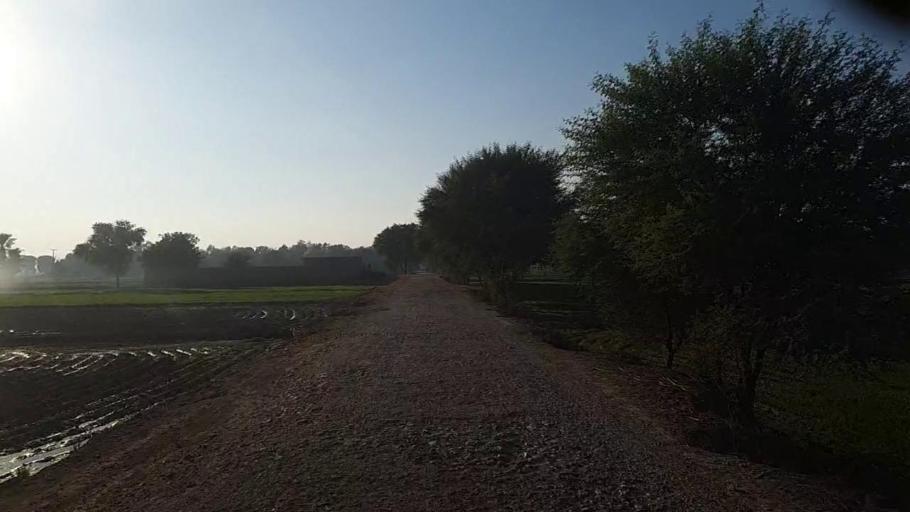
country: PK
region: Sindh
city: Pad Idan
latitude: 26.7342
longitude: 68.3321
